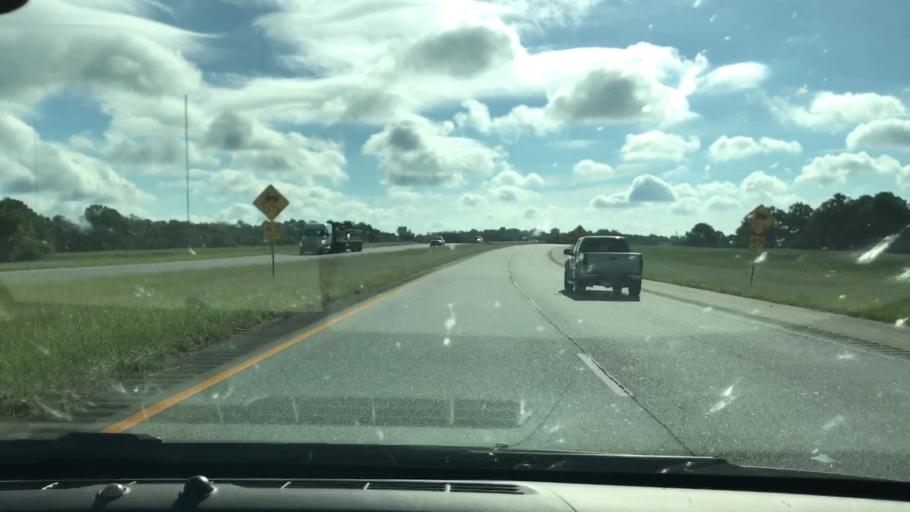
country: US
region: Georgia
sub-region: Dougherty County
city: Albany
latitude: 31.6166
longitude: -84.1791
